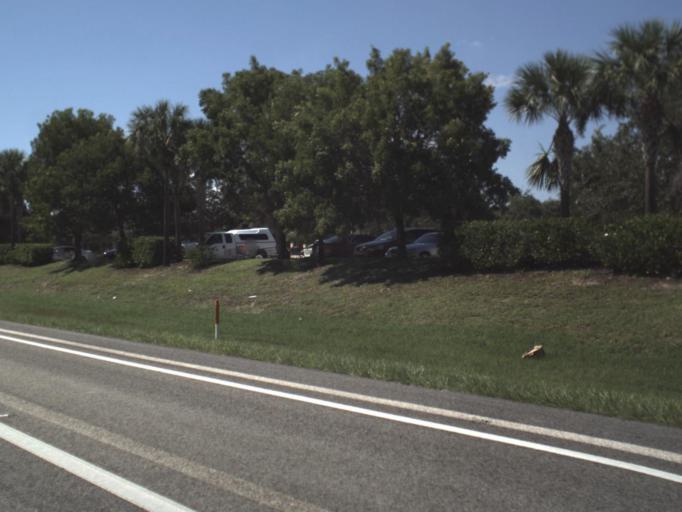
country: US
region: Florida
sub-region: Lee County
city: Lochmoor Waterway Estates
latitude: 26.6724
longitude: -81.9317
